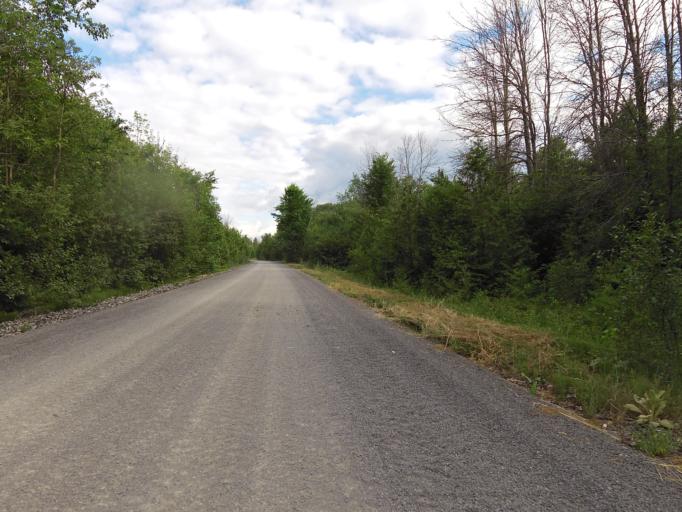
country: CA
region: Ontario
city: Arnprior
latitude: 45.2968
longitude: -76.2622
